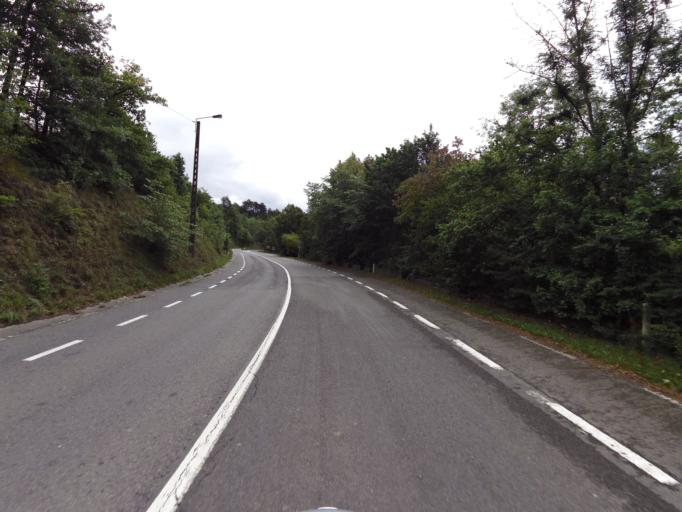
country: BE
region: Wallonia
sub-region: Province de Namur
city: Rochefort
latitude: 50.1307
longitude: 5.1881
